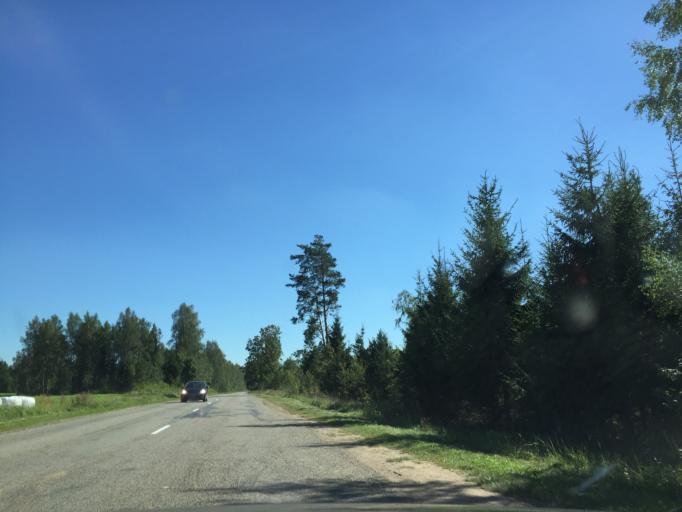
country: LV
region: Akniste
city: Akniste
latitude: 56.0764
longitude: 25.8835
